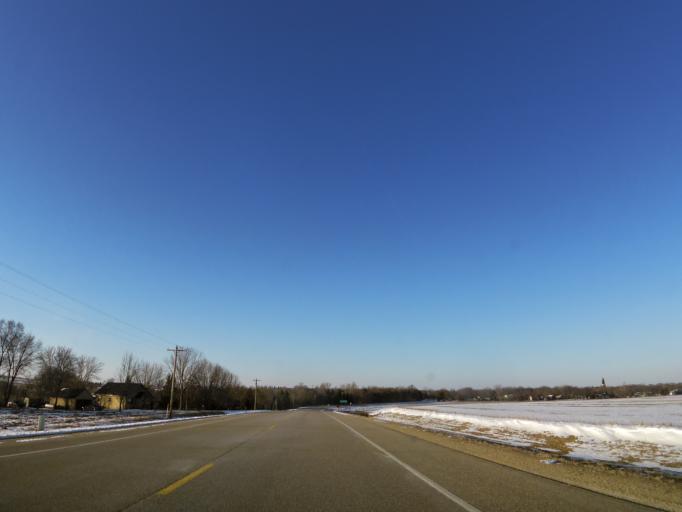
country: US
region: Minnesota
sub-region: Dakota County
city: Hastings
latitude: 44.6652
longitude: -92.9746
